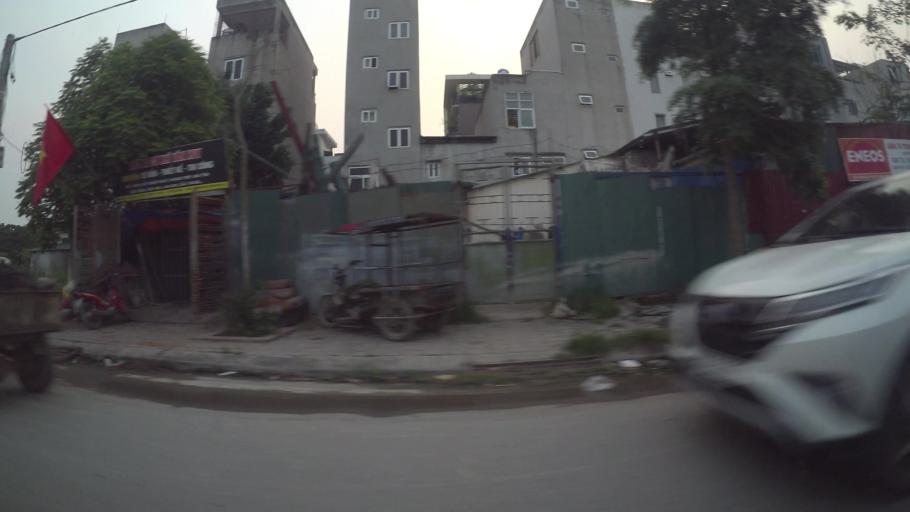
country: VN
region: Ha Noi
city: Thanh Xuan
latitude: 20.9775
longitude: 105.7990
